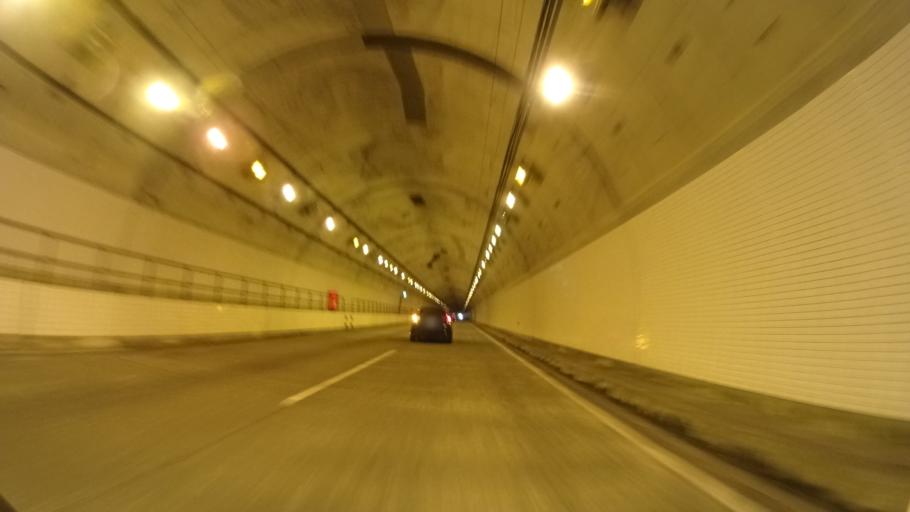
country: JP
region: Kumamoto
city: Yatsushiro
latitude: 32.4913
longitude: 130.6464
